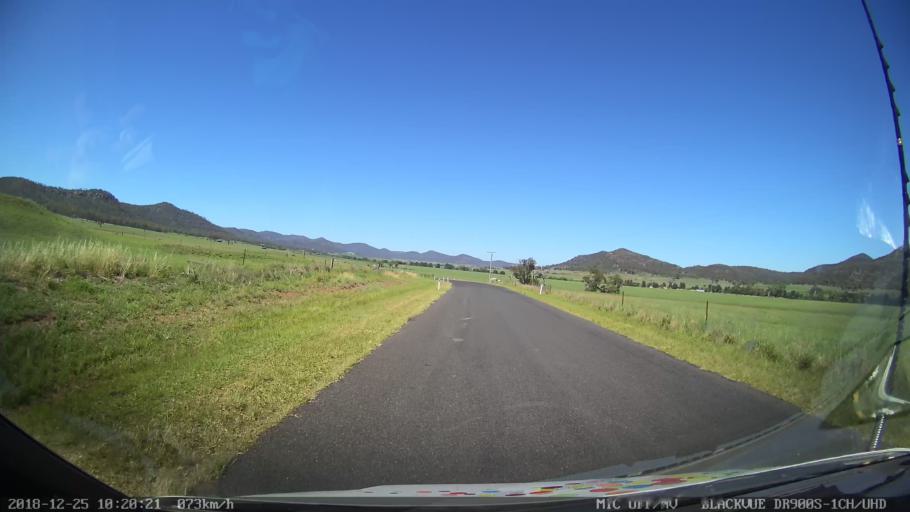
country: AU
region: New South Wales
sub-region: Muswellbrook
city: Denman
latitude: -32.3575
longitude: 150.5496
